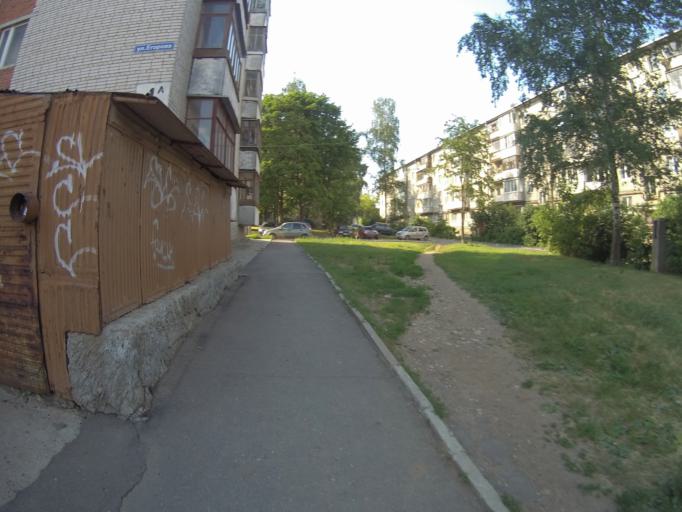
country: RU
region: Vladimir
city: Bogolyubovo
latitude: 56.1666
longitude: 40.4801
